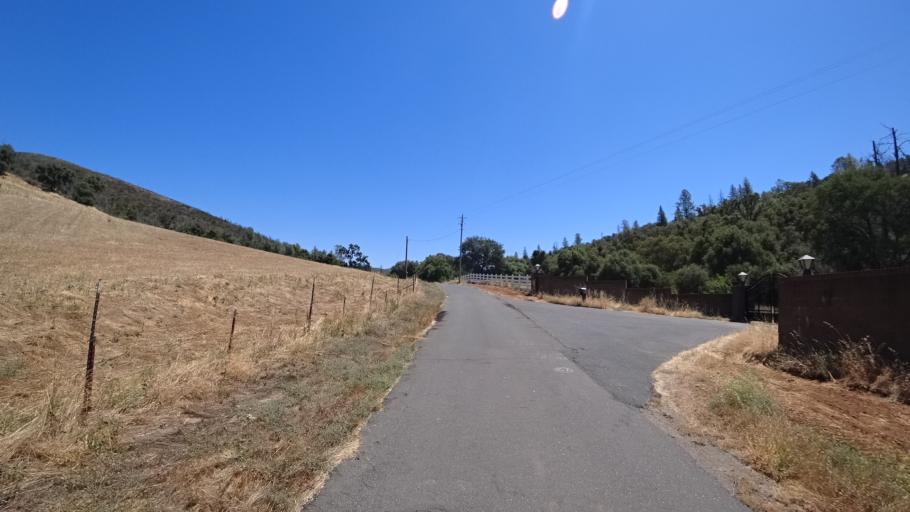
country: US
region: California
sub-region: Calaveras County
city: Mountain Ranch
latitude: 38.1806
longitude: -120.5839
